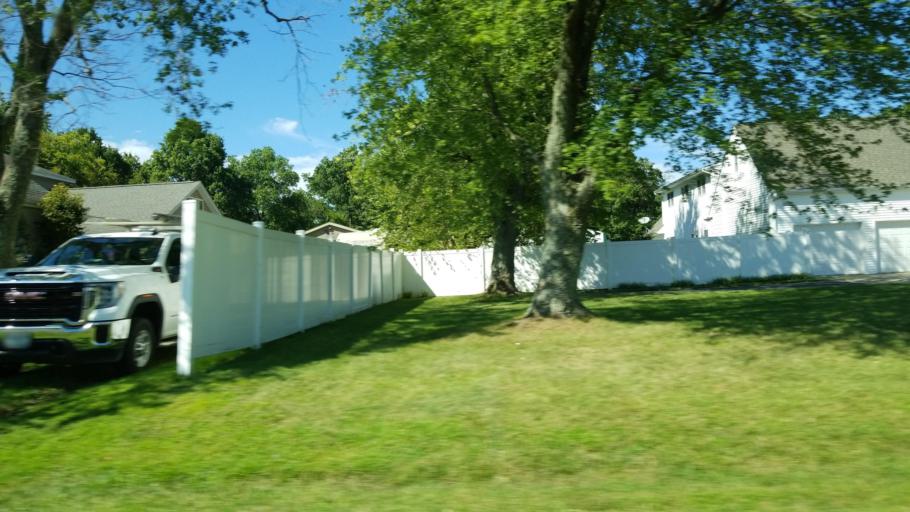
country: US
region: Illinois
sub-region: Williamson County
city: Marion
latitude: 37.7445
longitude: -88.8873
